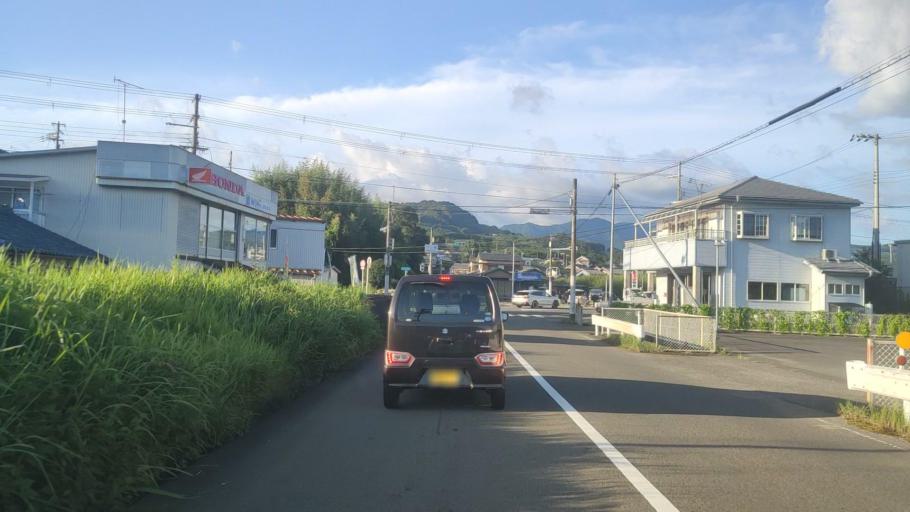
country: JP
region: Wakayama
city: Tanabe
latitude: 33.7345
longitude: 135.4187
